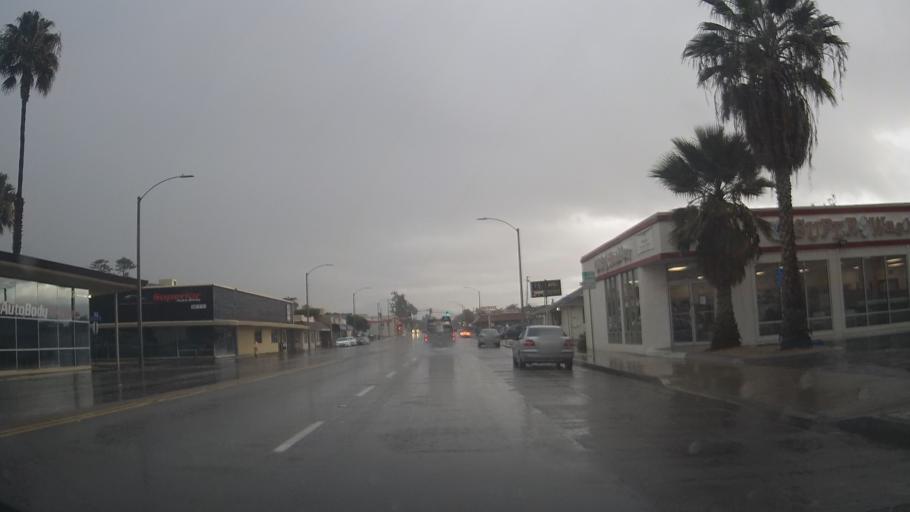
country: US
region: California
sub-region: San Diego County
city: Chula Vista
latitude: 32.6440
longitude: -117.0834
